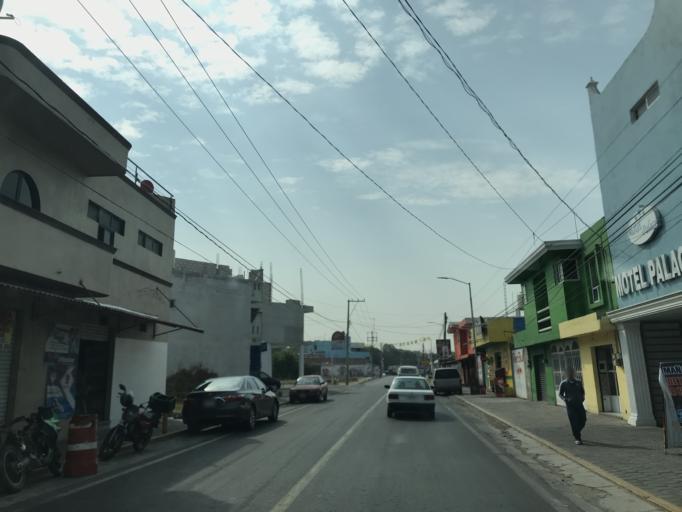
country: MX
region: Tlaxcala
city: Tenancingo
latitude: 19.1430
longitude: -98.1929
